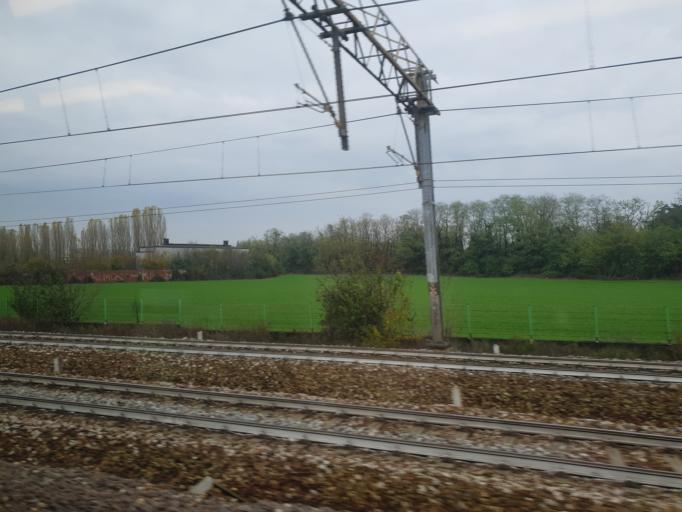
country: IT
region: Lombardy
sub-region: Citta metropolitana di Milano
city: Novate Milanese
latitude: 45.5222
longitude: 9.1425
